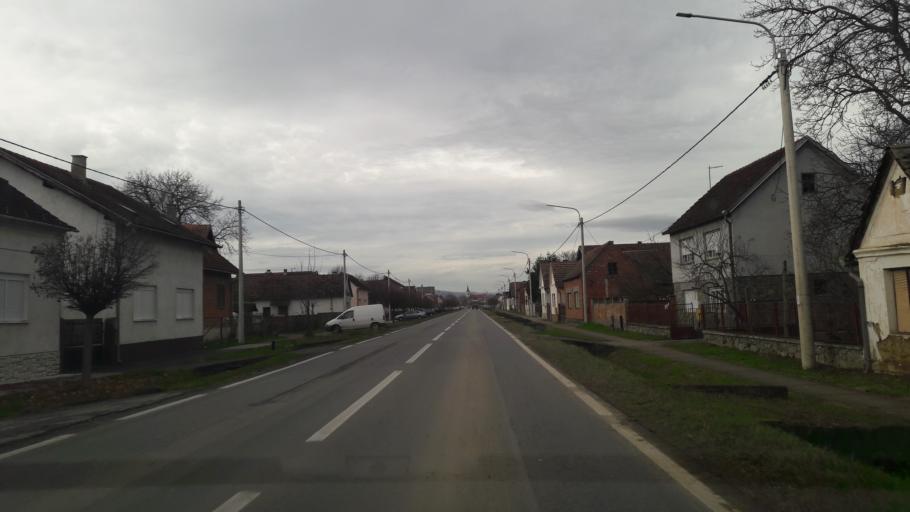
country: HR
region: Osjecko-Baranjska
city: Fericanci
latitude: 45.5237
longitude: 17.9906
